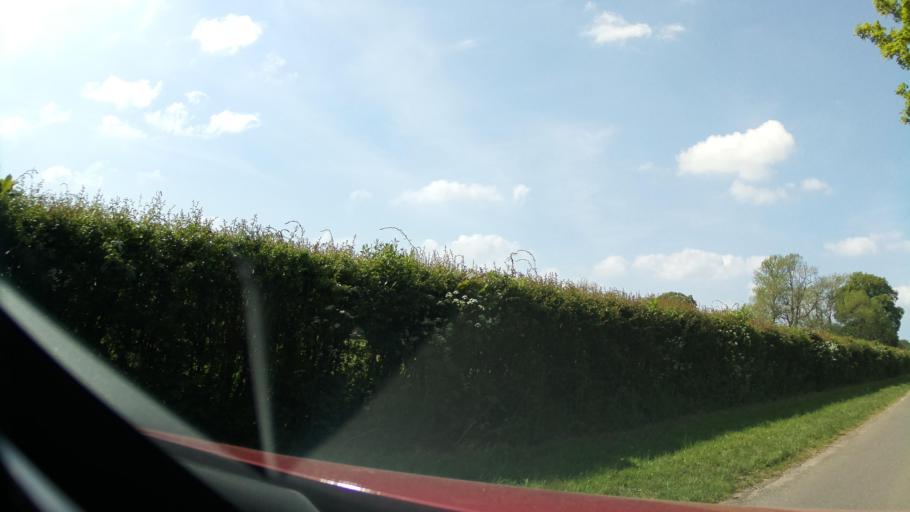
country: GB
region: England
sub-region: Wiltshire
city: Luckington
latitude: 51.5791
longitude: -2.2712
